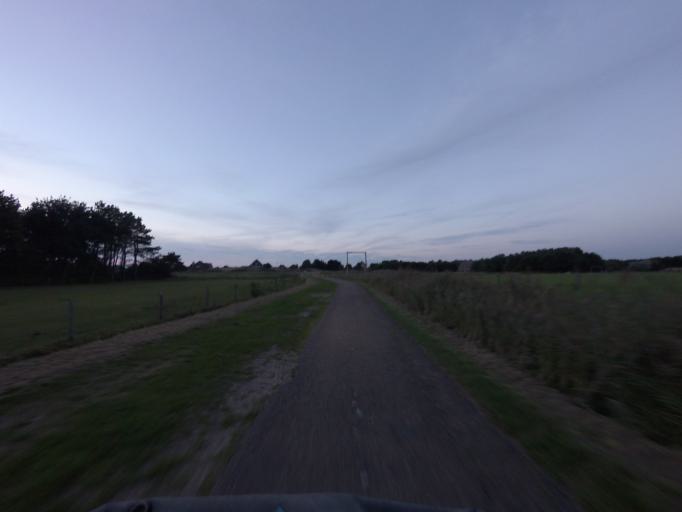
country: NL
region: Friesland
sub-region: Gemeente Ameland
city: Nes
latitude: 53.4538
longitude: 5.7961
